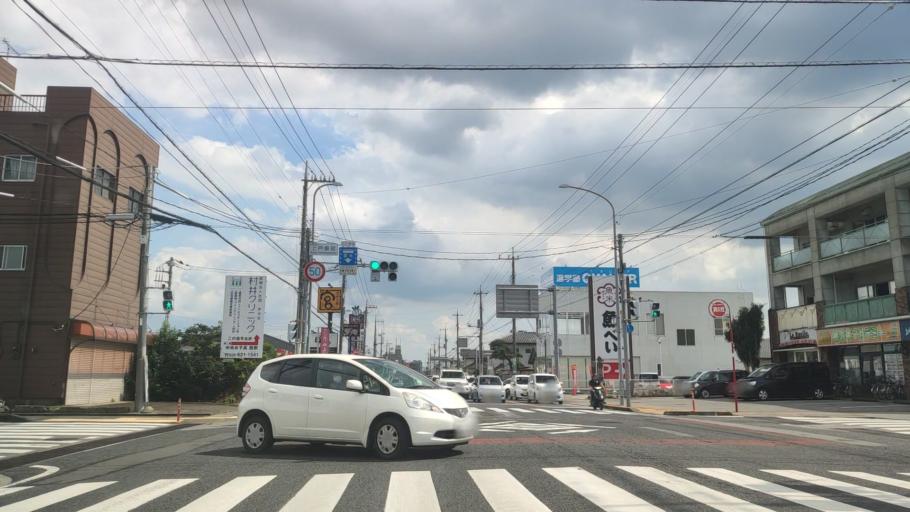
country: JP
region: Tochigi
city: Utsunomiya-shi
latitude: 36.5860
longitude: 139.8660
